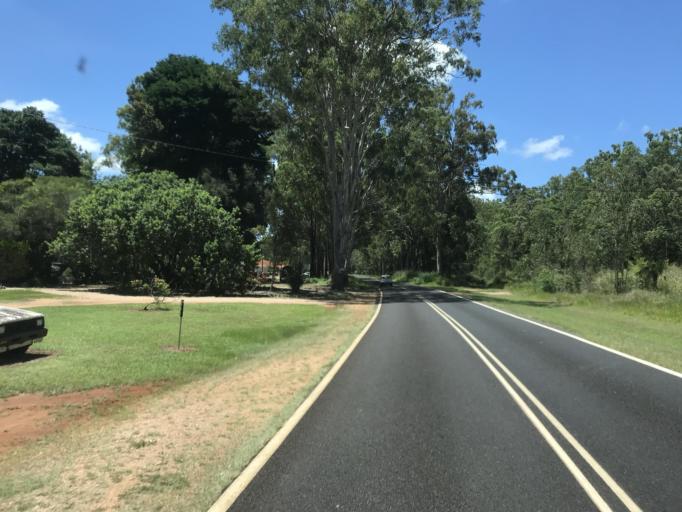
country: AU
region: Queensland
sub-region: Tablelands
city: Atherton
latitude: -17.4257
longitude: 145.3983
